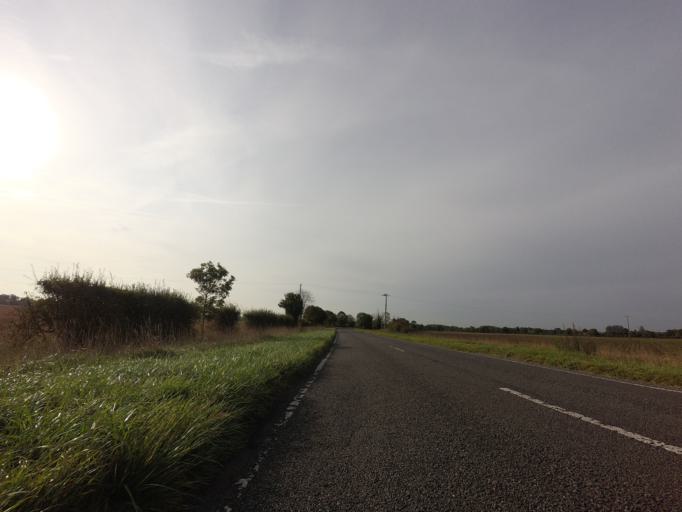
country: GB
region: England
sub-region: Cambridgeshire
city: Harston
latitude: 52.1018
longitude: 0.0840
